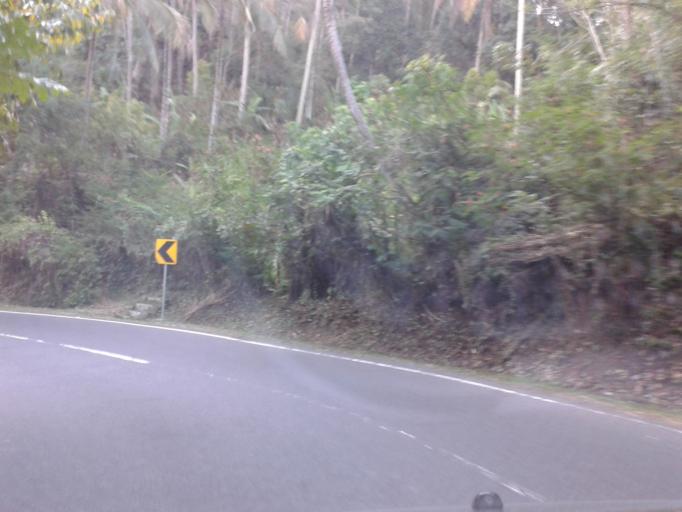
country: ID
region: Bali
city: Banjar Wangsian
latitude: -8.4802
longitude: 115.4001
